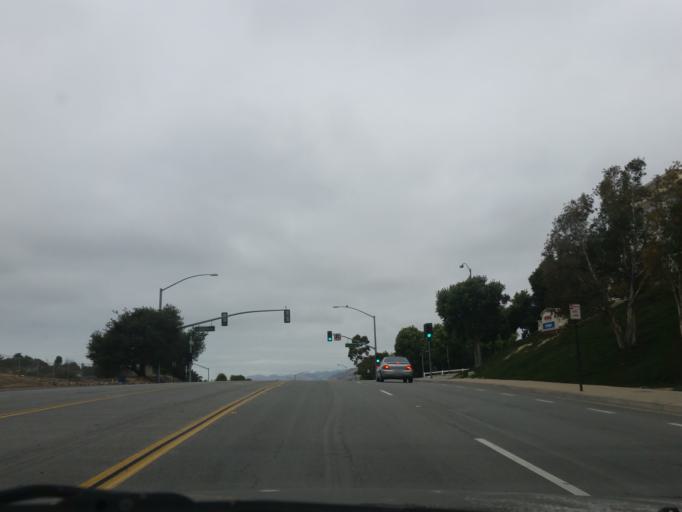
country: US
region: California
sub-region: San Luis Obispo County
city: Arroyo Grande
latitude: 35.1256
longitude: -120.5948
